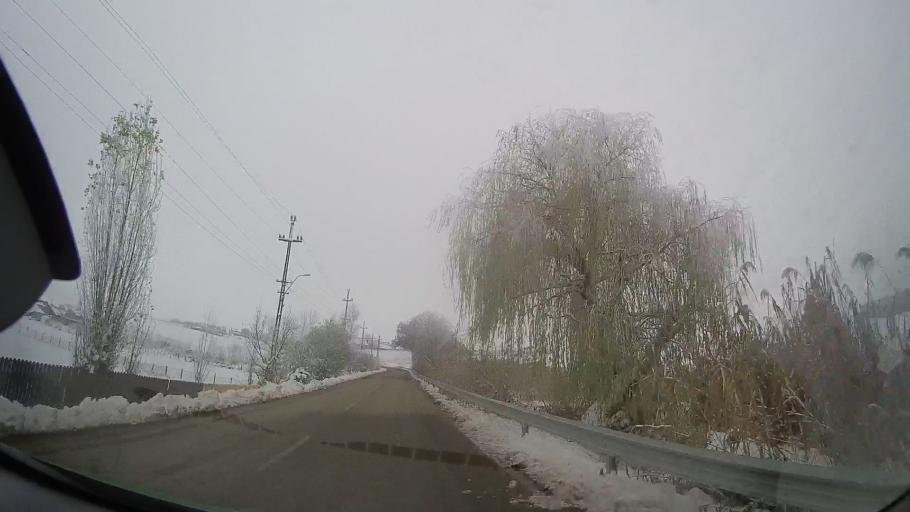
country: RO
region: Iasi
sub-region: Comuna Dagata
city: Dagata
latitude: 46.9170
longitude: 27.1972
